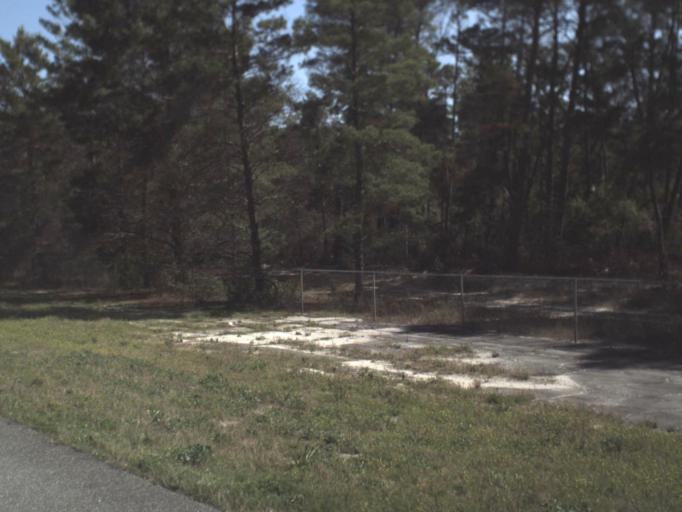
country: US
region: Florida
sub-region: Franklin County
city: Carrabelle
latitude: 29.9316
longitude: -84.4386
